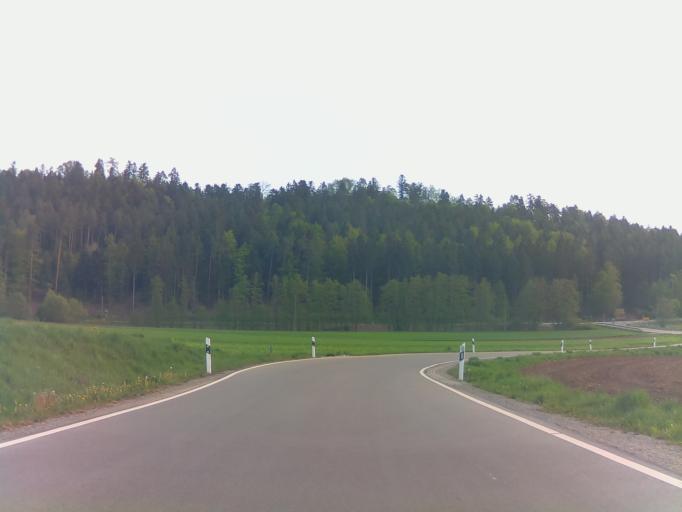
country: DE
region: Baden-Wuerttemberg
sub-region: Freiburg Region
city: Muhlheim am Bach
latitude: 48.3408
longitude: 8.7324
